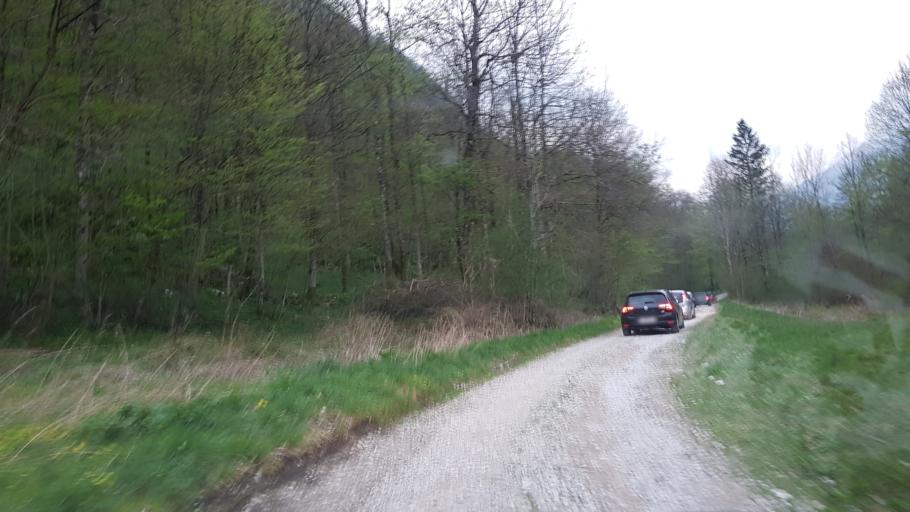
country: SI
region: Kobarid
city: Kobarid
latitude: 46.2401
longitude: 13.5347
